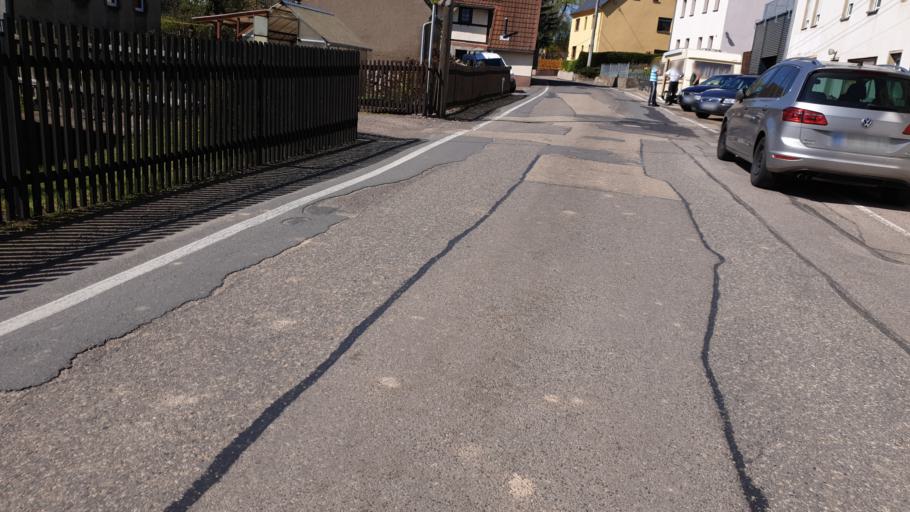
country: DE
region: Saxony
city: Taura
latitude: 50.9088
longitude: 12.8707
